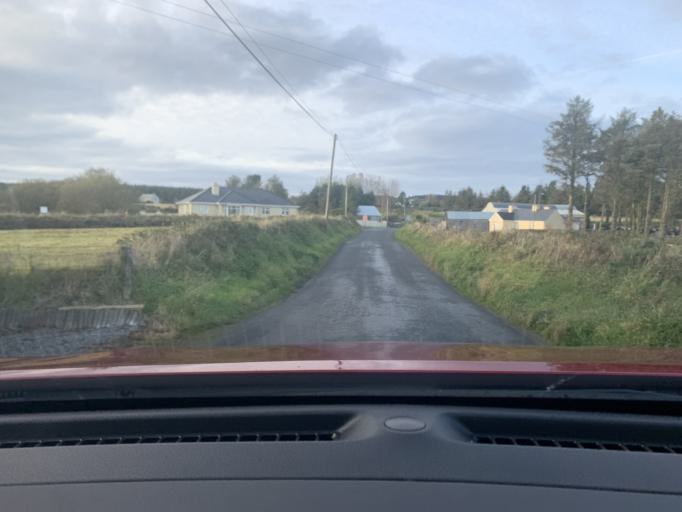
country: IE
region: Connaught
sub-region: Roscommon
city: Ballaghaderreen
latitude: 53.9155
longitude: -8.5902
